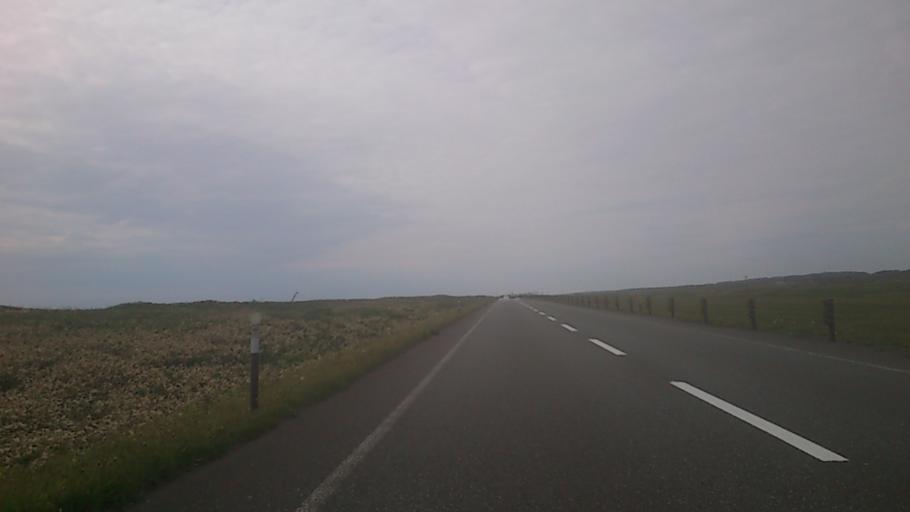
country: JP
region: Hokkaido
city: Wakkanai
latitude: 45.0658
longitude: 141.6437
